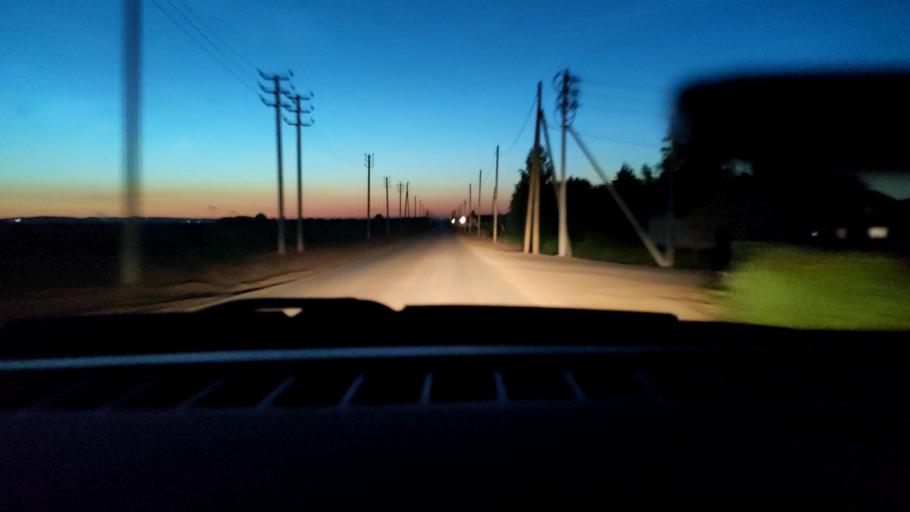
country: RU
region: Perm
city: Kultayevo
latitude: 57.8733
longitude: 55.9866
